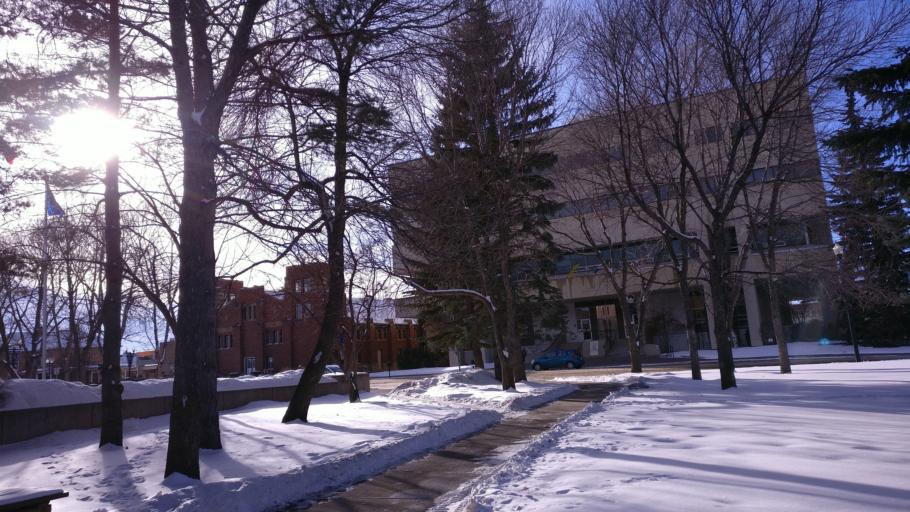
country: CA
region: Alberta
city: Red Deer
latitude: 52.2688
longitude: -113.8084
